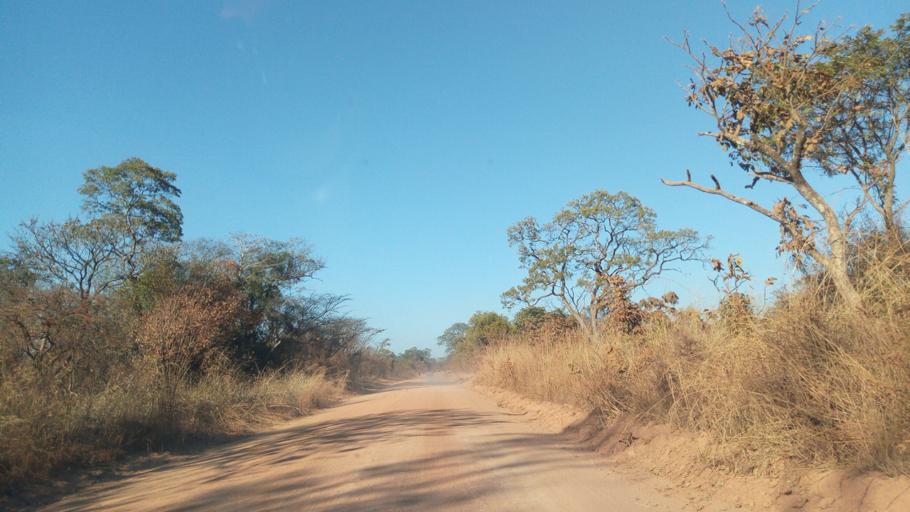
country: ZM
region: Luapula
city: Mwense
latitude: -10.5281
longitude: 28.4546
